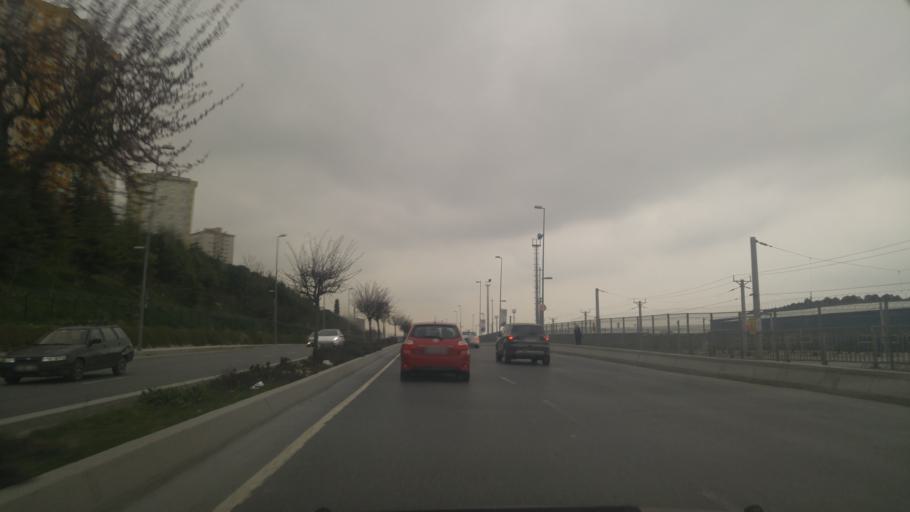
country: TR
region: Istanbul
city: Mahmutbey
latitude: 41.0283
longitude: 28.7678
